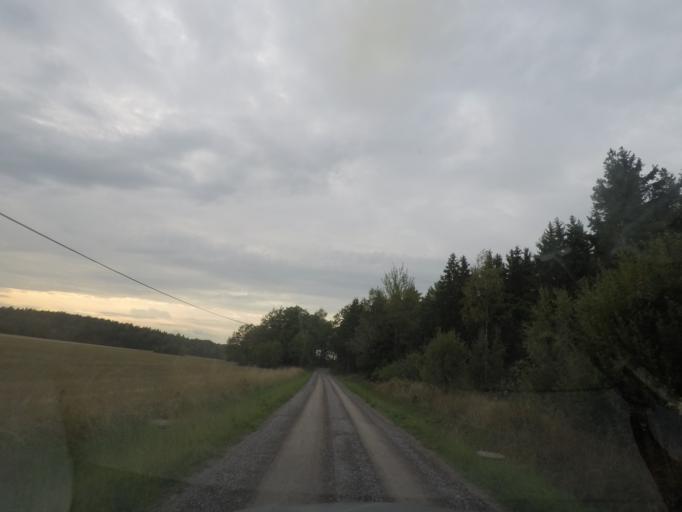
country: SE
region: Vaestmanland
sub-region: Hallstahammars Kommun
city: Kolback
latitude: 59.4799
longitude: 16.1944
